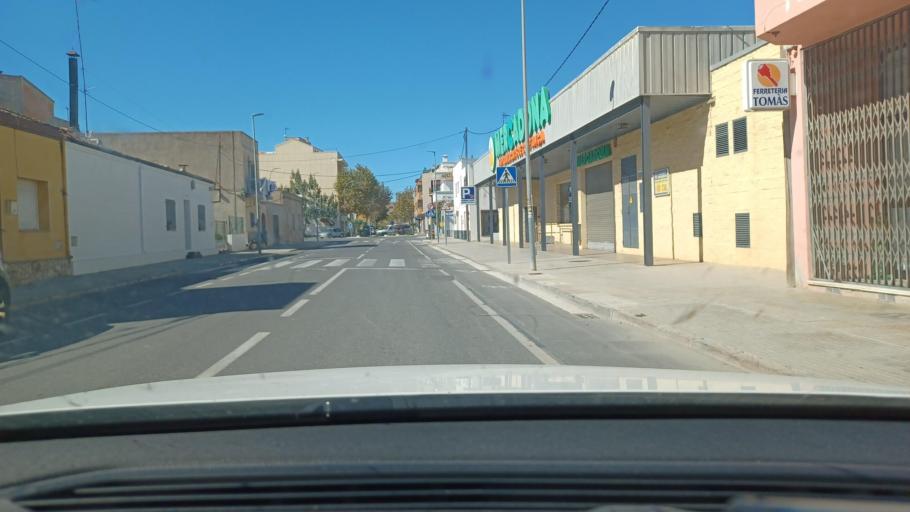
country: ES
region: Catalonia
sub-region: Provincia de Tarragona
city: Deltebre
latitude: 40.7196
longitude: 0.7305
